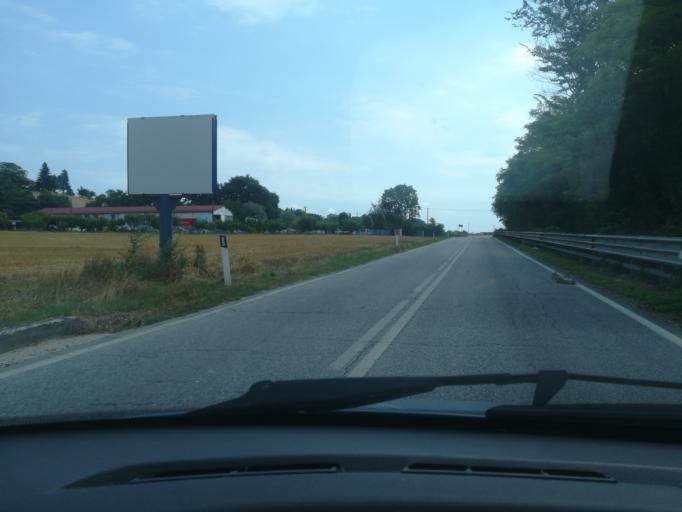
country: IT
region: The Marches
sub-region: Provincia di Macerata
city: Sforzacosta
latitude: 43.2621
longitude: 13.4378
